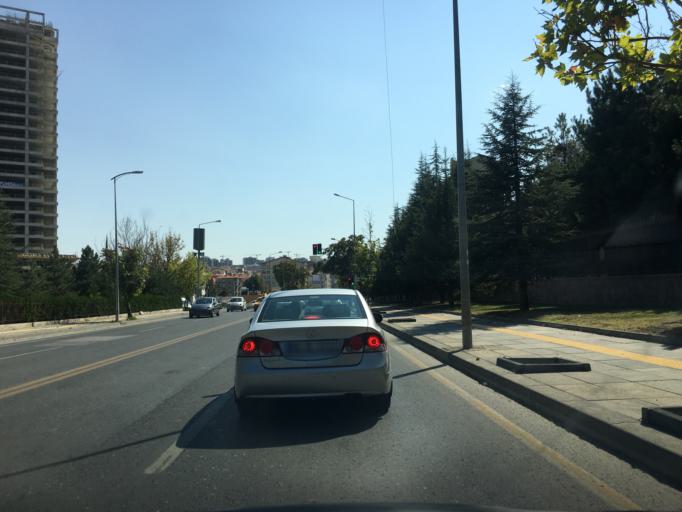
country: TR
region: Ankara
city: Cankaya
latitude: 39.8801
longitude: 32.8658
